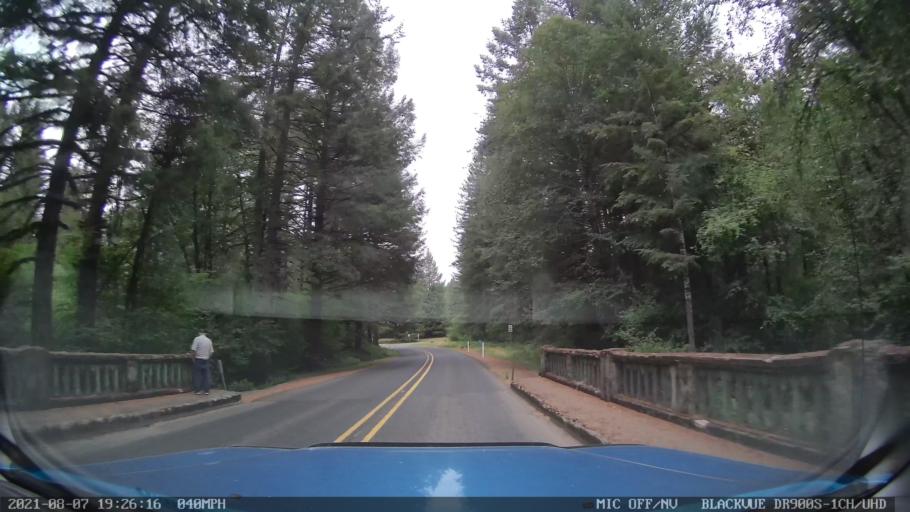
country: US
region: Oregon
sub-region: Linn County
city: Lyons
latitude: 44.8703
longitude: -122.6525
